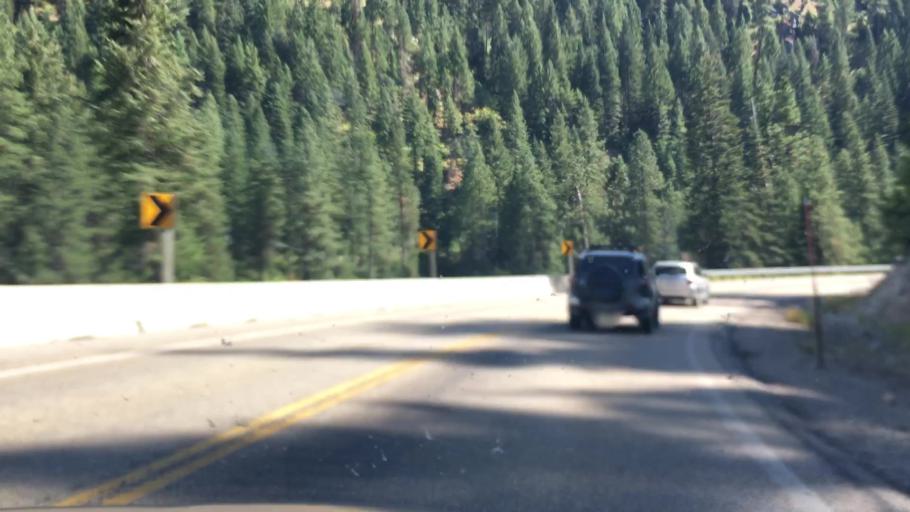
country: US
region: Idaho
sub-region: Valley County
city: Cascade
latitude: 44.1787
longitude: -116.1147
